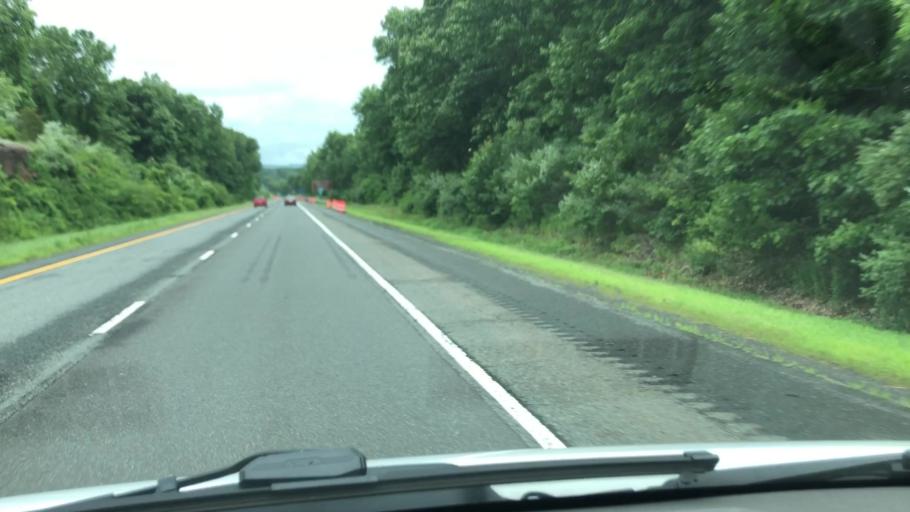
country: US
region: Massachusetts
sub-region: Franklin County
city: Greenfield
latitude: 42.5547
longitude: -72.6203
